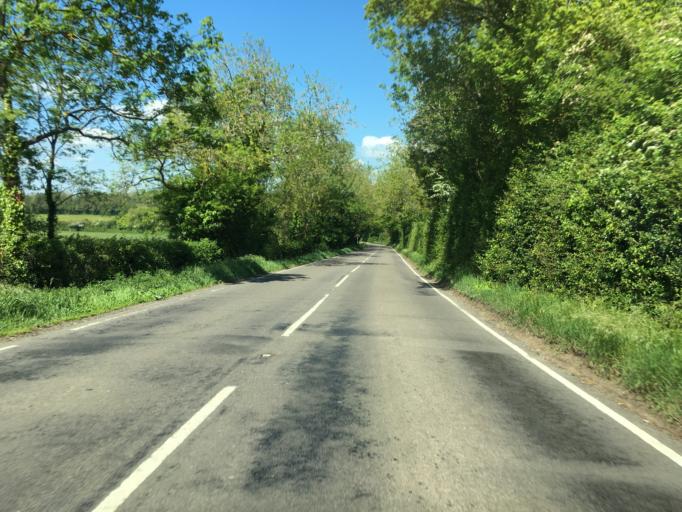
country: GB
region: England
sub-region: Buckinghamshire
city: Buckingham
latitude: 52.0183
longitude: -1.0542
